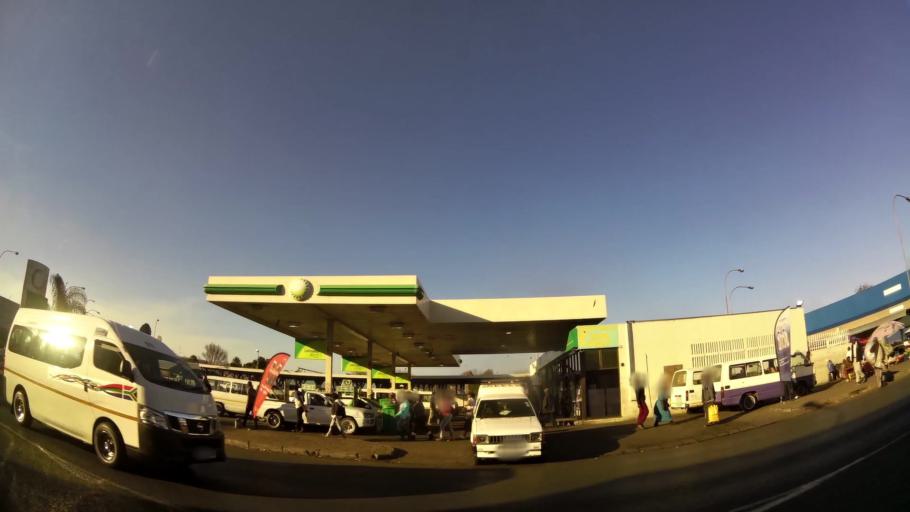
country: ZA
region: Gauteng
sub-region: City of Johannesburg Metropolitan Municipality
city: Roodepoort
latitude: -26.1608
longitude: 27.8697
